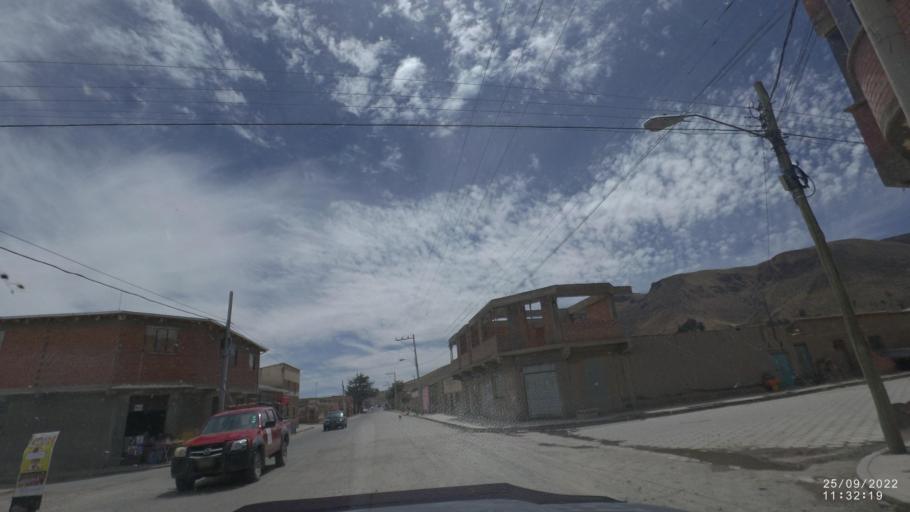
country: BO
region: Oruro
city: Challapata
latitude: -19.0159
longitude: -66.7771
